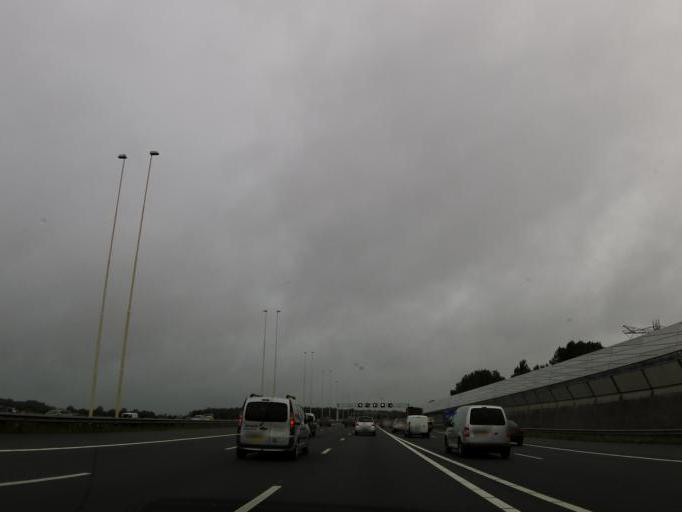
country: NL
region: Utrecht
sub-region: Stichtse Vecht
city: Spechtenkamp
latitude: 52.1266
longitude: 5.0181
